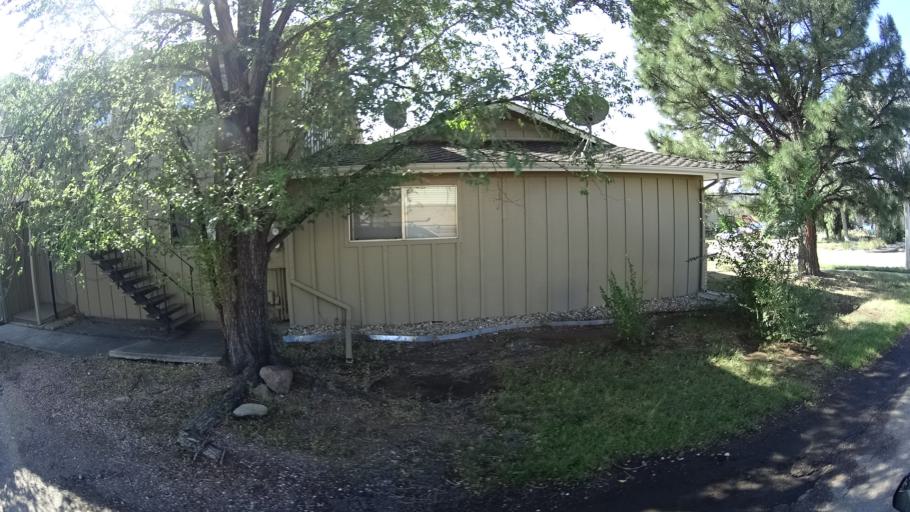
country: US
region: Colorado
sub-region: El Paso County
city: Colorado Springs
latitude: 38.8934
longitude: -104.8434
